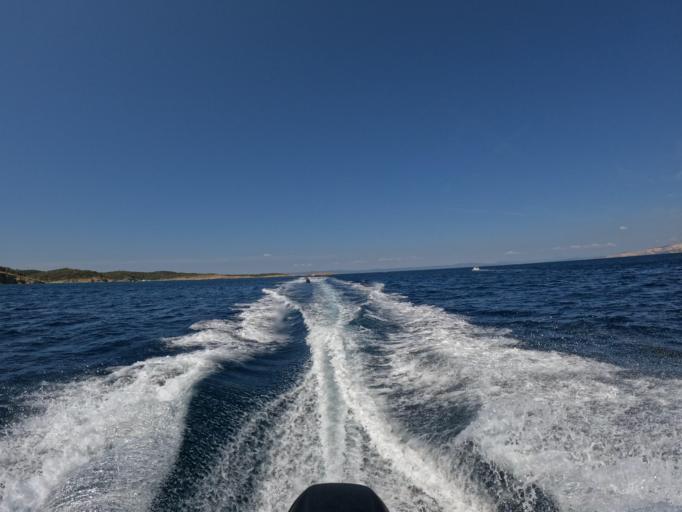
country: HR
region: Primorsko-Goranska
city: Lopar
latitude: 44.8525
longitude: 14.7472
